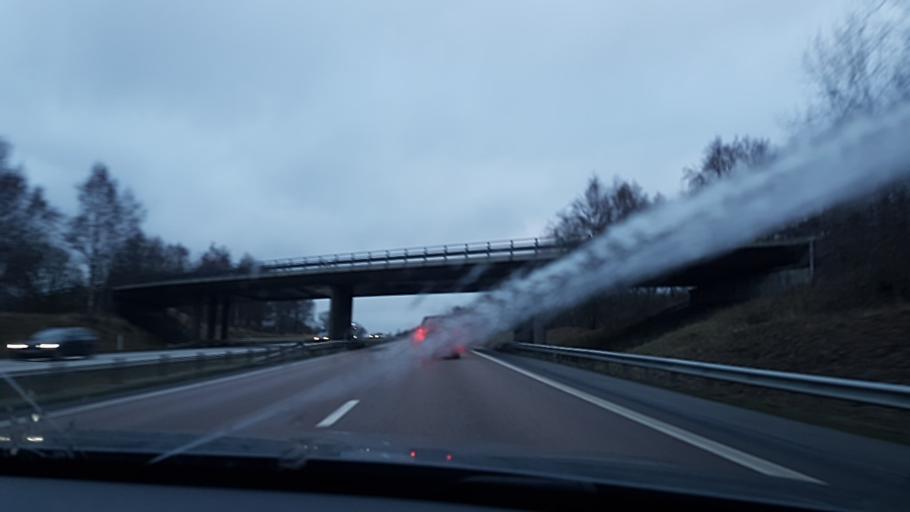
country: SE
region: Skane
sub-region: Helsingborg
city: Gantofta
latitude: 56.0169
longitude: 12.7811
